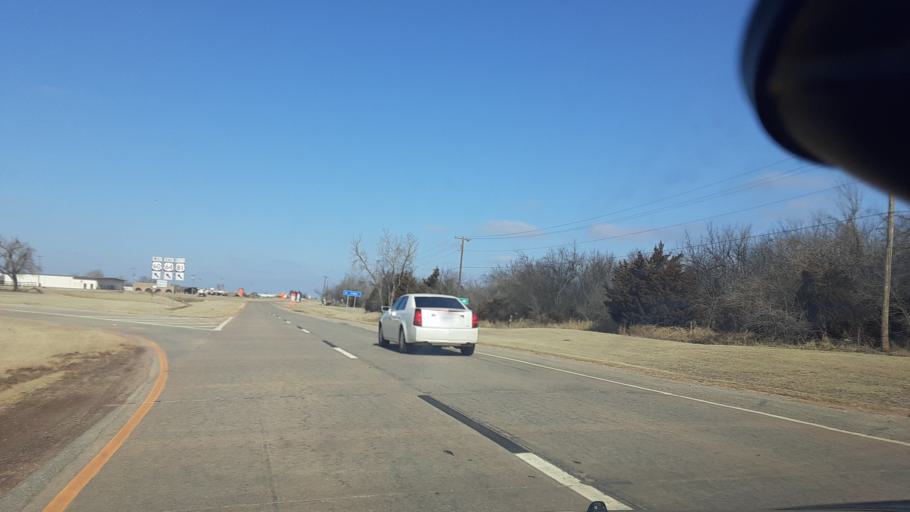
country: US
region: Oklahoma
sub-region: Garfield County
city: Enid
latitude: 36.4467
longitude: -97.8723
